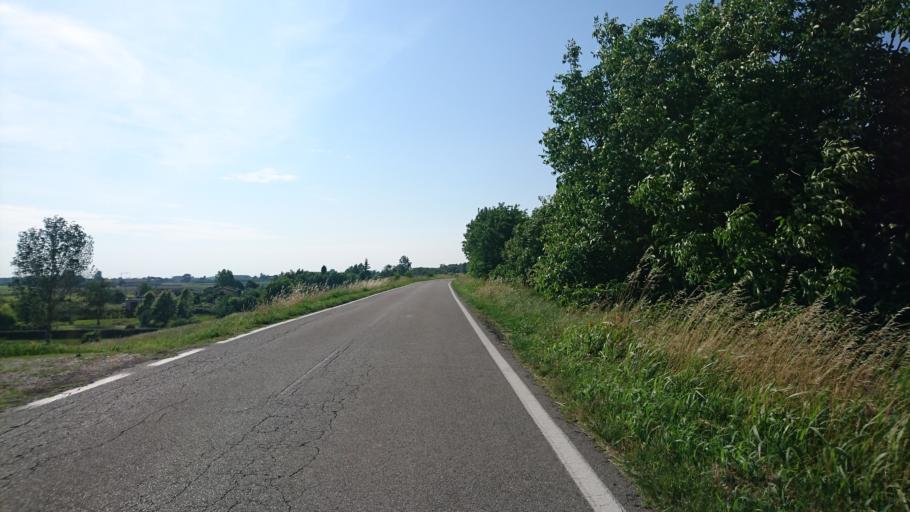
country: IT
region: Veneto
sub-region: Provincia di Verona
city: Villa Bartolomea
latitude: 45.1704
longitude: 11.3483
